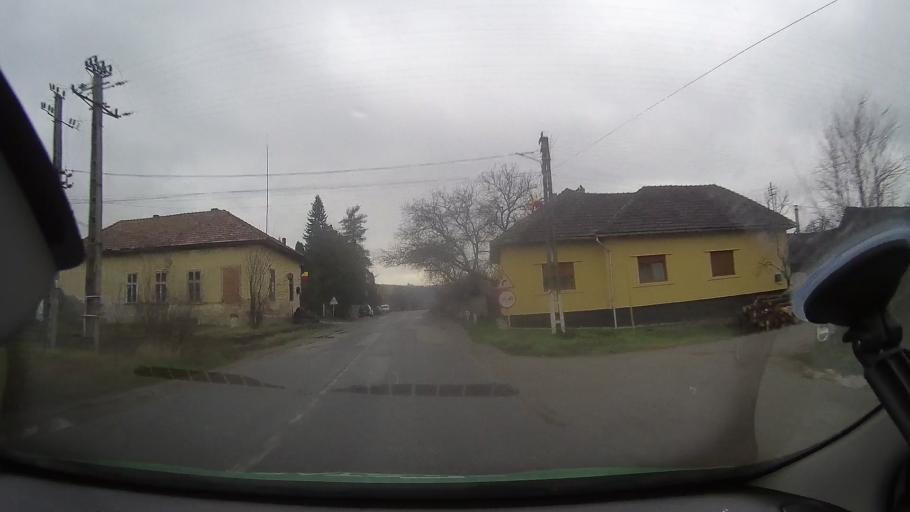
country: RO
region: Arad
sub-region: Comuna Halmagiu
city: Halmagiu
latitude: 46.2680
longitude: 22.5970
